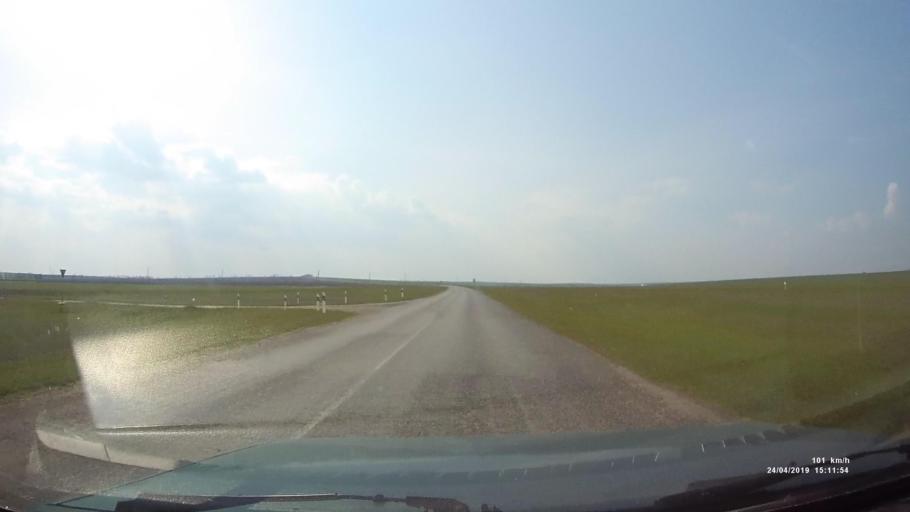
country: RU
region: Rostov
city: Remontnoye
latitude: 46.5452
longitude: 43.3126
